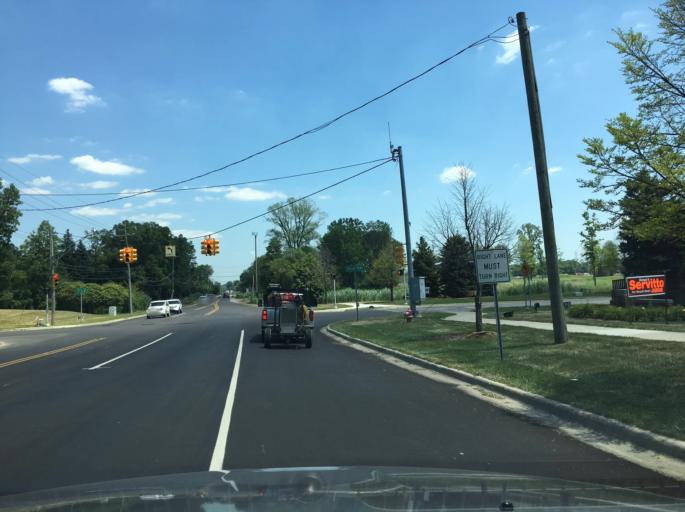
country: US
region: Michigan
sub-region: Macomb County
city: Shelby
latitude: 42.6841
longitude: -83.0153
